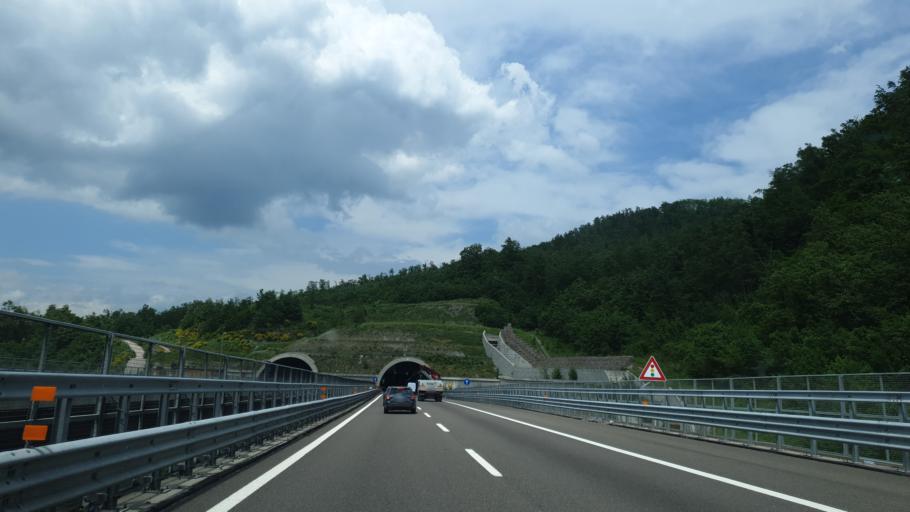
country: IT
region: Emilia-Romagna
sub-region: Provincia di Bologna
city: San Benedetto Val di Sambro
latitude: 44.1929
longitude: 11.2004
